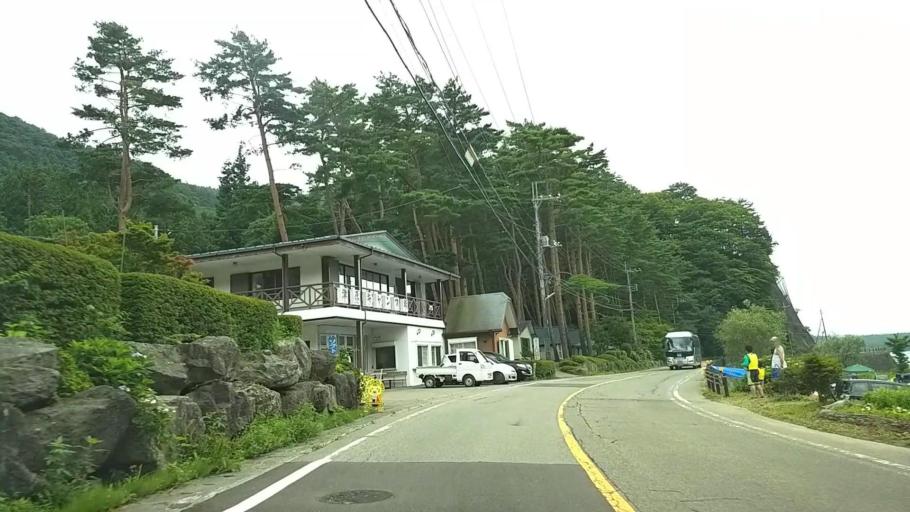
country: JP
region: Yamanashi
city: Fujikawaguchiko
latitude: 35.4992
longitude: 138.6990
